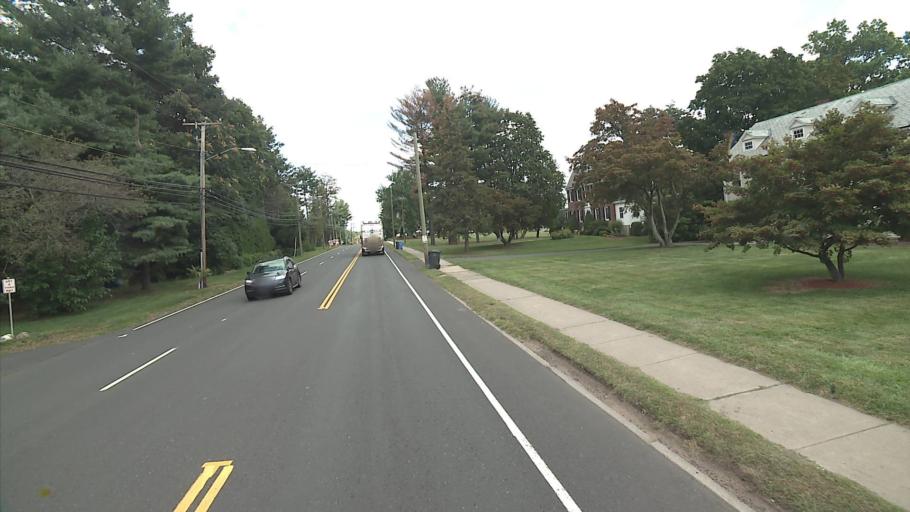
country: US
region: Connecticut
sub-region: Hartford County
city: Blue Hills
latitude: 41.7912
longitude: -72.7153
